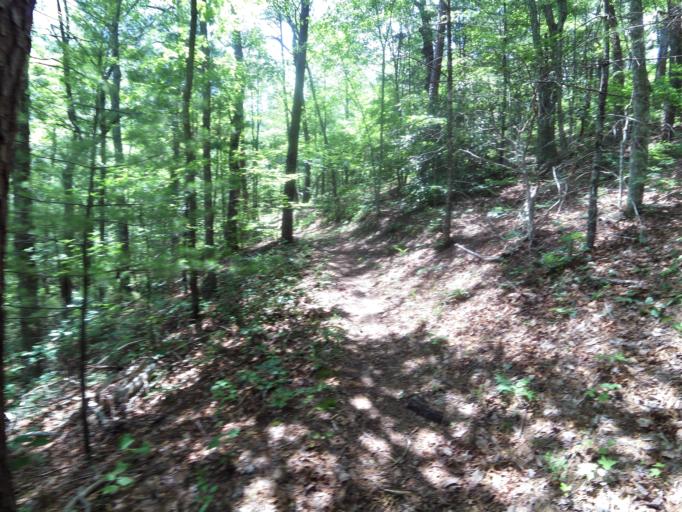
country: US
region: Tennessee
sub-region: Blount County
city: Wildwood
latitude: 35.6692
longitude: -83.8380
